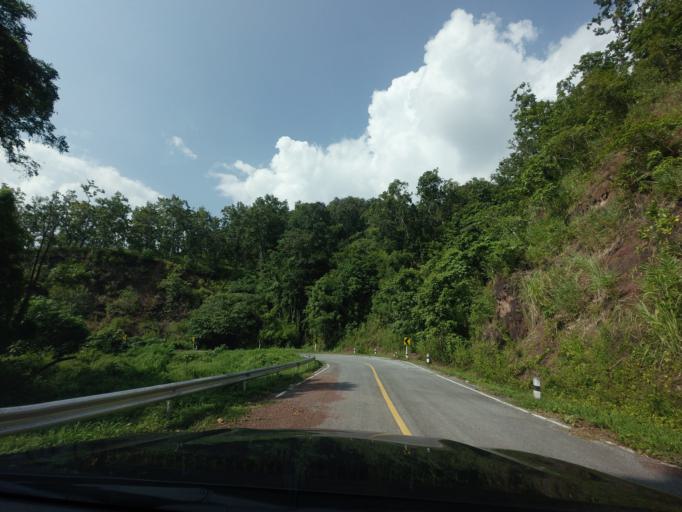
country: TH
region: Uttaradit
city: Ban Khok
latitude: 18.2495
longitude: 100.9980
